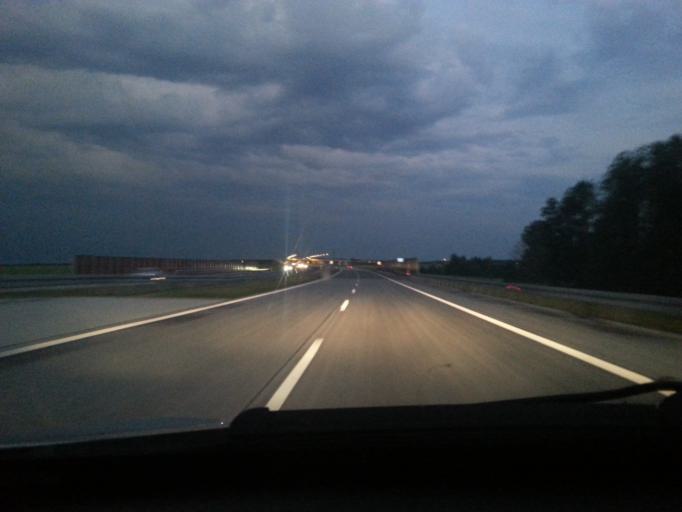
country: PL
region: Lodz Voivodeship
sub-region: Powiat sieradzki
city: Sieradz
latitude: 51.5392
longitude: 18.6974
